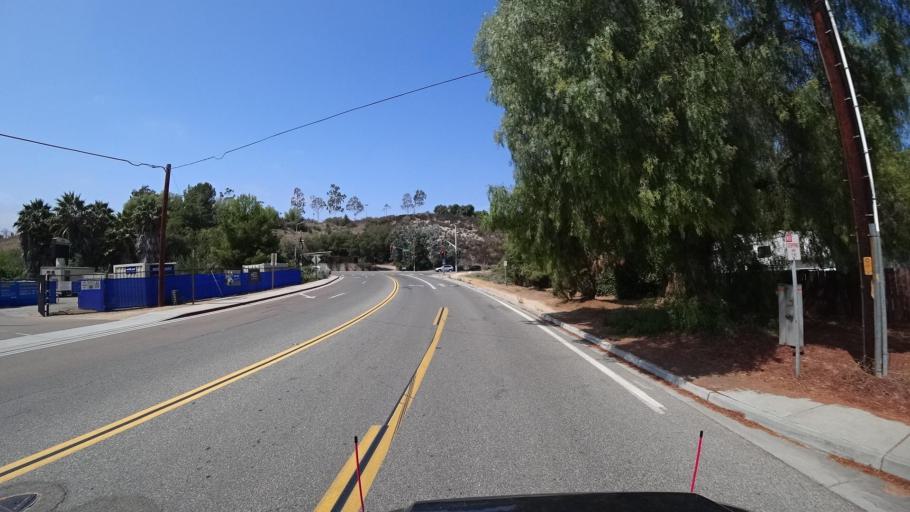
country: US
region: California
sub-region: San Diego County
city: Fallbrook
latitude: 33.3496
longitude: -117.2435
